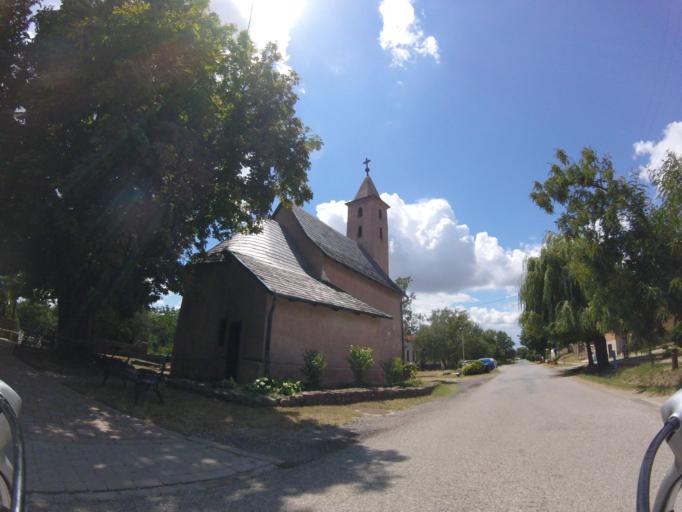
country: HU
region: Baranya
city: Pellerd
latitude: 46.0758
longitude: 18.1342
